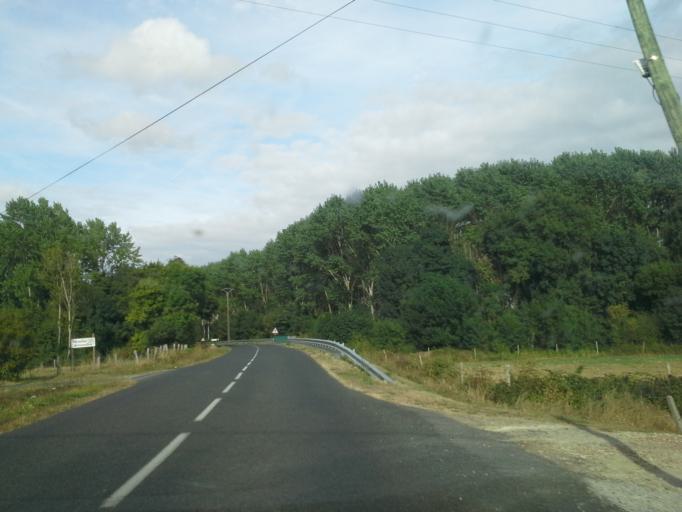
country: FR
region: Centre
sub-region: Departement d'Indre-et-Loire
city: Auzouer-en-Touraine
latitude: 47.5225
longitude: 0.9184
